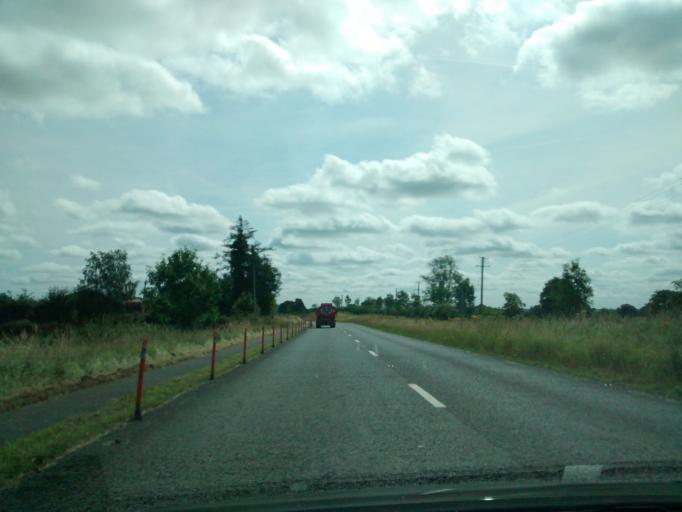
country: IE
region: Leinster
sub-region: An Iarmhi
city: Moate
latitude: 53.3834
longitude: -7.6783
